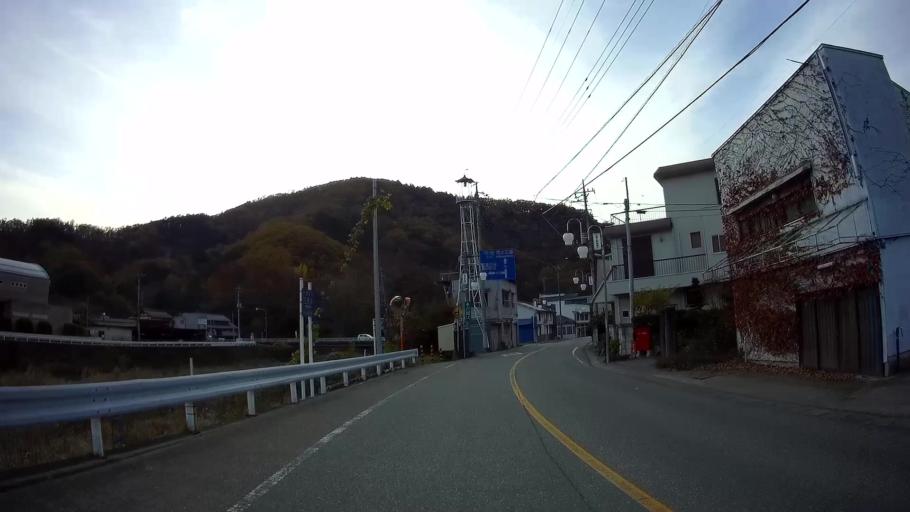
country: JP
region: Yamanashi
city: Ryuo
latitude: 35.4802
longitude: 138.4715
